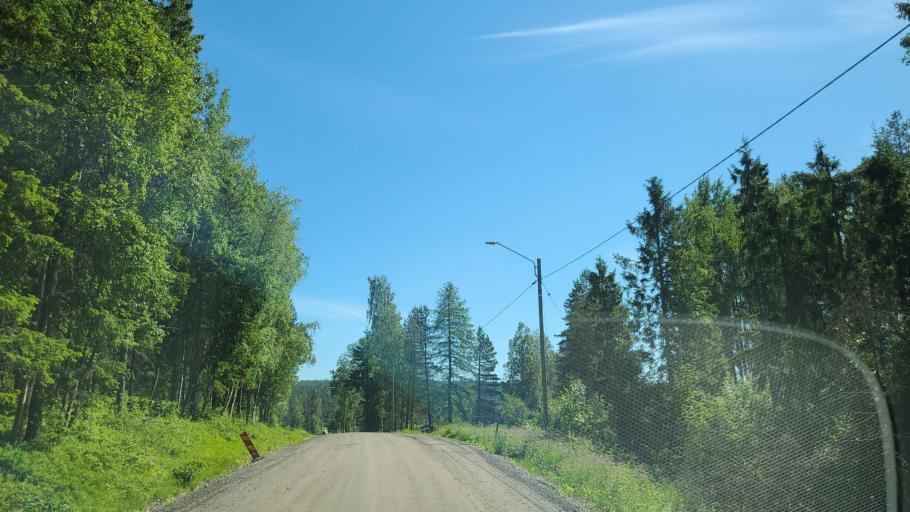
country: SE
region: Vaesterbotten
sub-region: Bjurholms Kommun
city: Bjurholm
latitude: 63.6460
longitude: 19.0909
